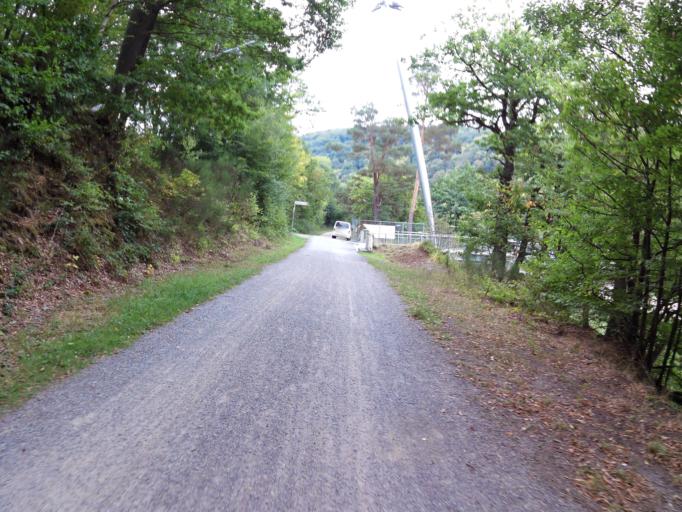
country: DE
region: North Rhine-Westphalia
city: Heimbach
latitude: 50.5930
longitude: 6.4529
